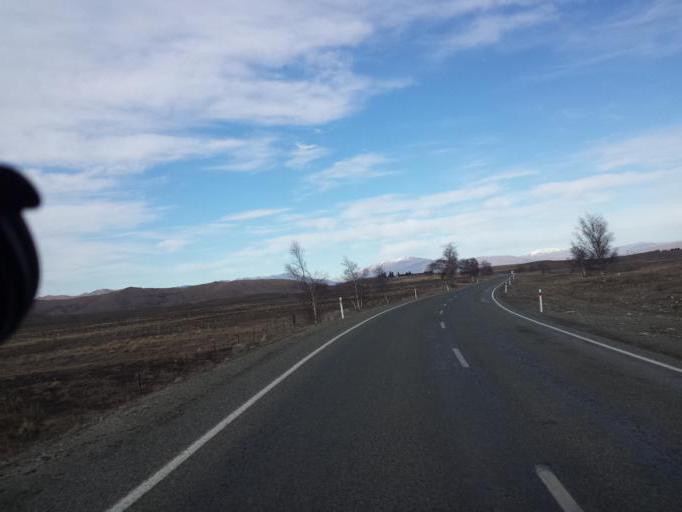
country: NZ
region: Canterbury
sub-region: Timaru District
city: Pleasant Point
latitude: -44.0207
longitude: 170.5012
